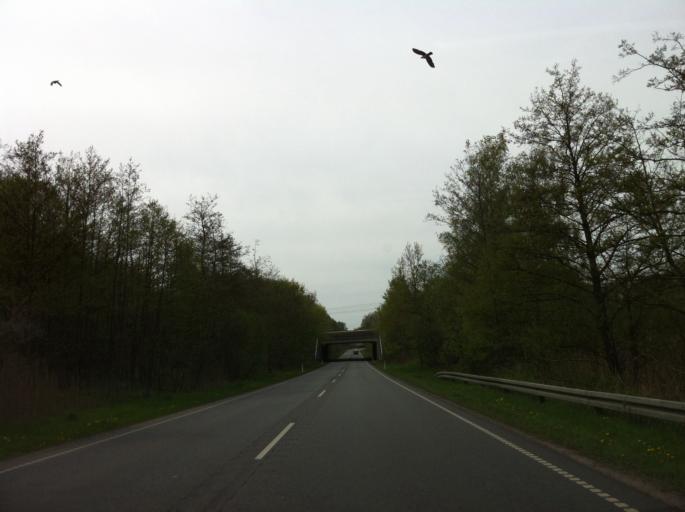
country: DK
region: Capital Region
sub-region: Hillerod Kommune
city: Hillerod
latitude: 55.9134
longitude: 12.3160
